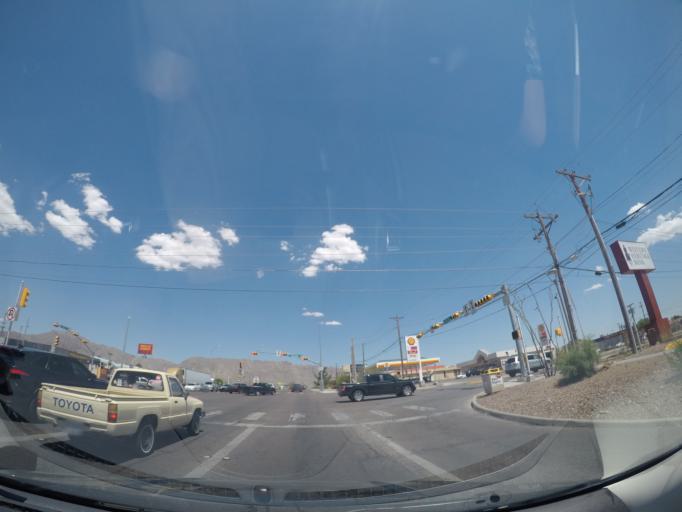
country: US
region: New Mexico
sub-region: Dona Ana County
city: Sunland Park
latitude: 31.8356
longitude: -106.5509
